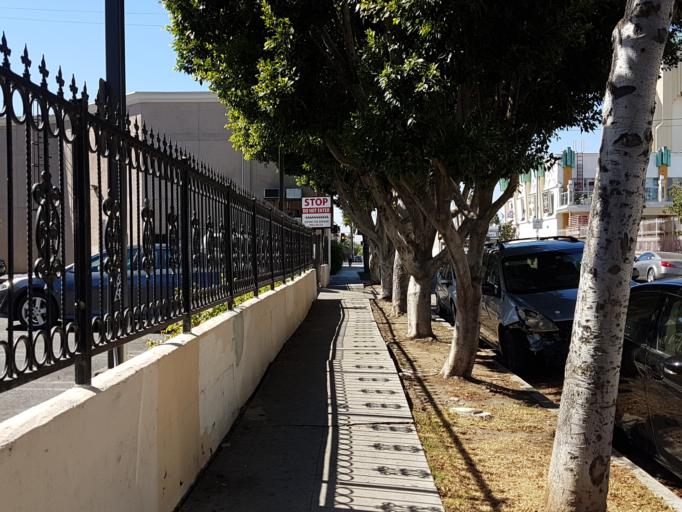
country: US
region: California
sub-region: Los Angeles County
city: Hollywood
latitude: 34.0671
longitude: -118.3081
